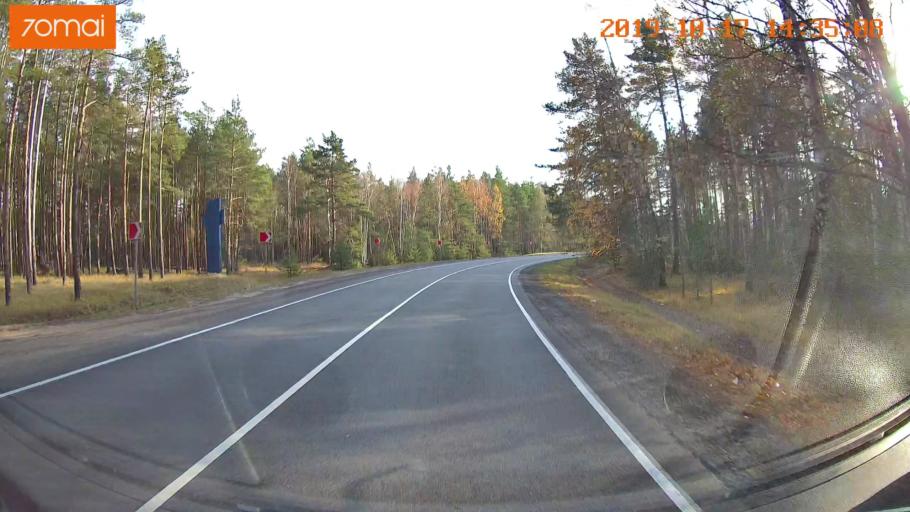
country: RU
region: Rjazan
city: Solotcha
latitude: 54.9037
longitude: 40.0032
